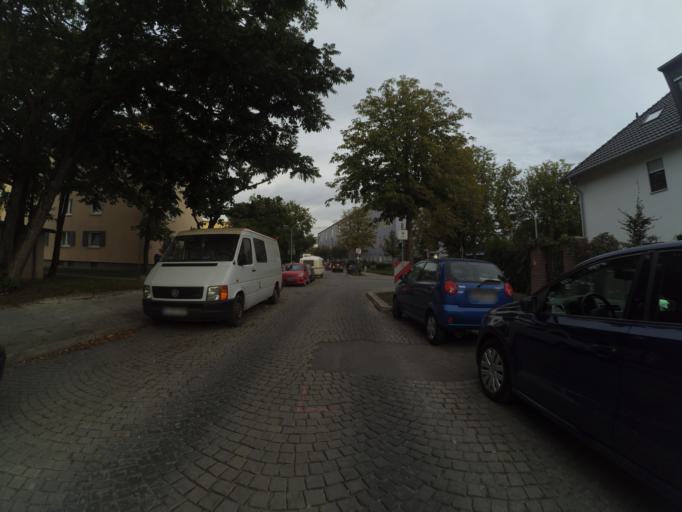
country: DE
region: Bavaria
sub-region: Upper Bavaria
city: Karlsfeld
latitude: 48.1755
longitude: 11.5135
